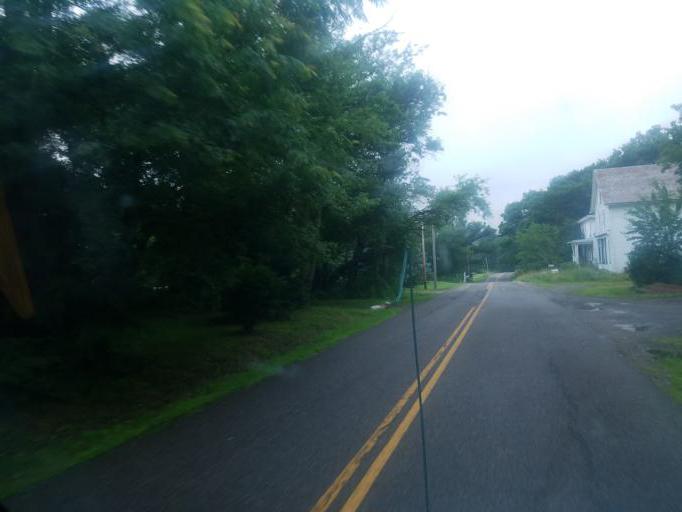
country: US
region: Ohio
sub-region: Columbiana County
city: Salineville
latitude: 40.5757
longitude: -80.9572
